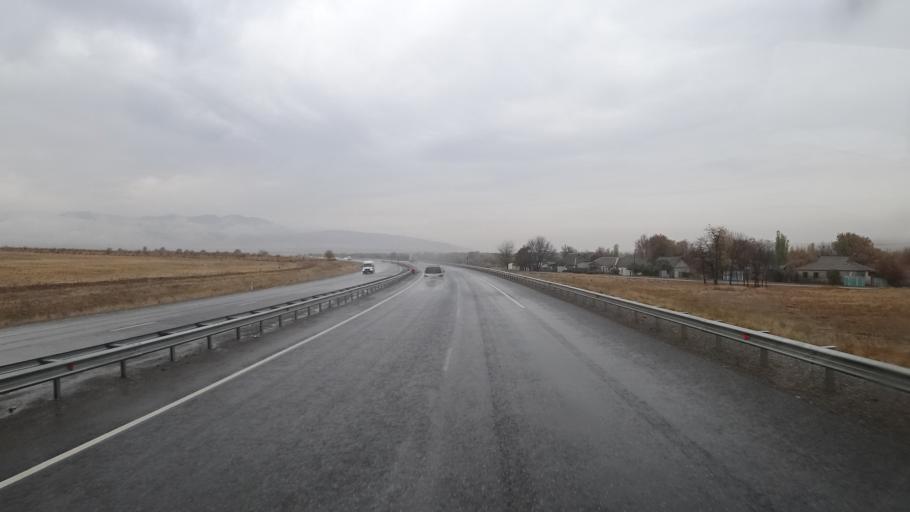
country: KZ
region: Ongtustik Qazaqstan
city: Kokterek
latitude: 42.5466
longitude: 70.2352
